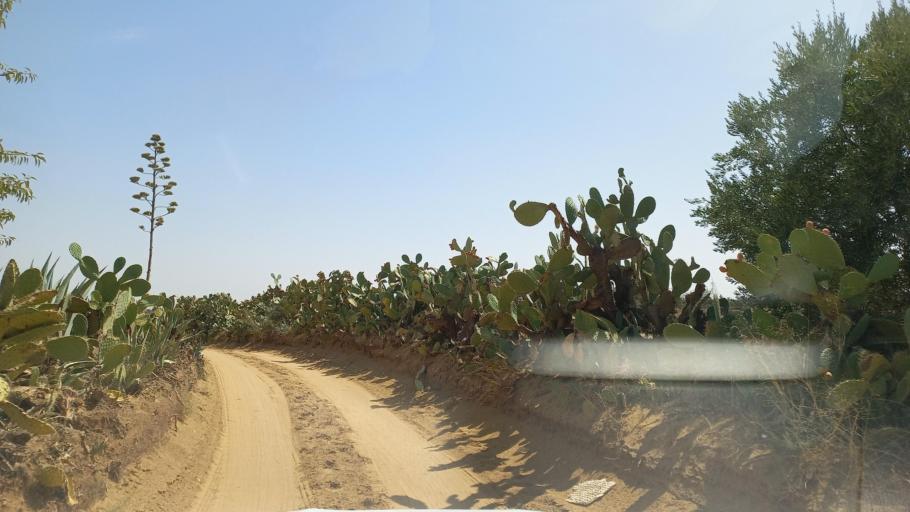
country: TN
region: Al Qasrayn
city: Kasserine
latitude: 35.2381
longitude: 9.0308
